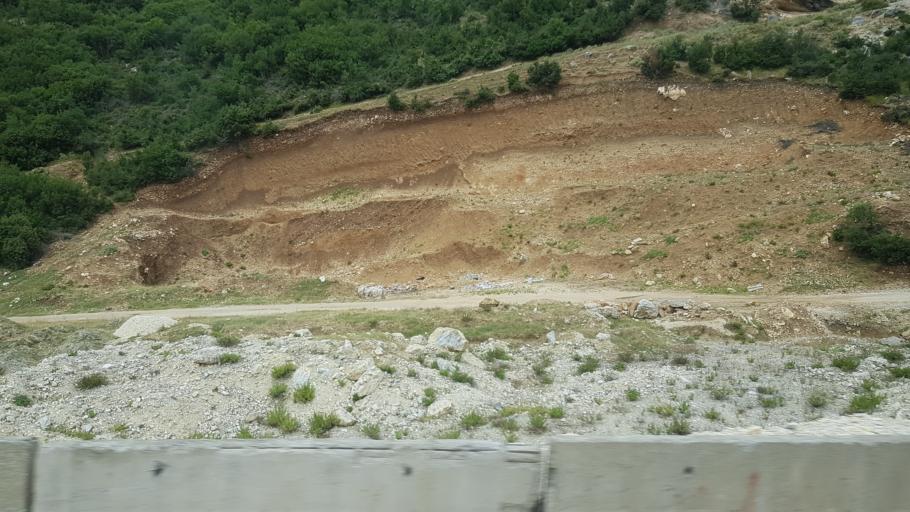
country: AL
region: Fier
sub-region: Rrethi i Mallakastres
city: Kute
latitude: 40.5100
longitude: 19.7523
